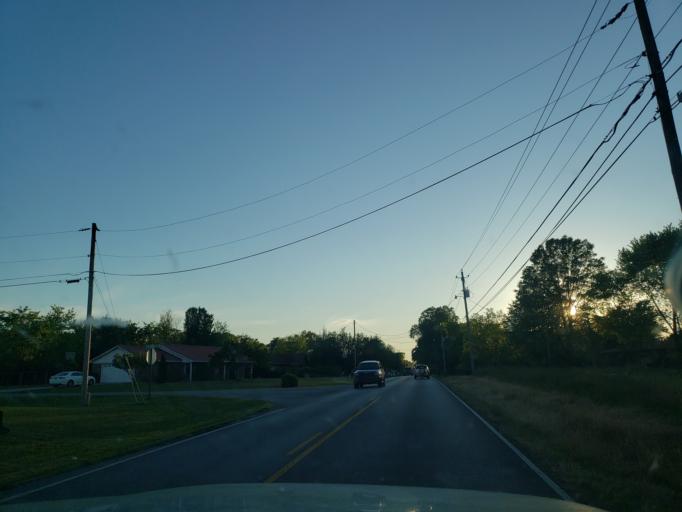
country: US
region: Alabama
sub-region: Madison County
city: Hazel Green
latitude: 34.9322
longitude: -86.5564
